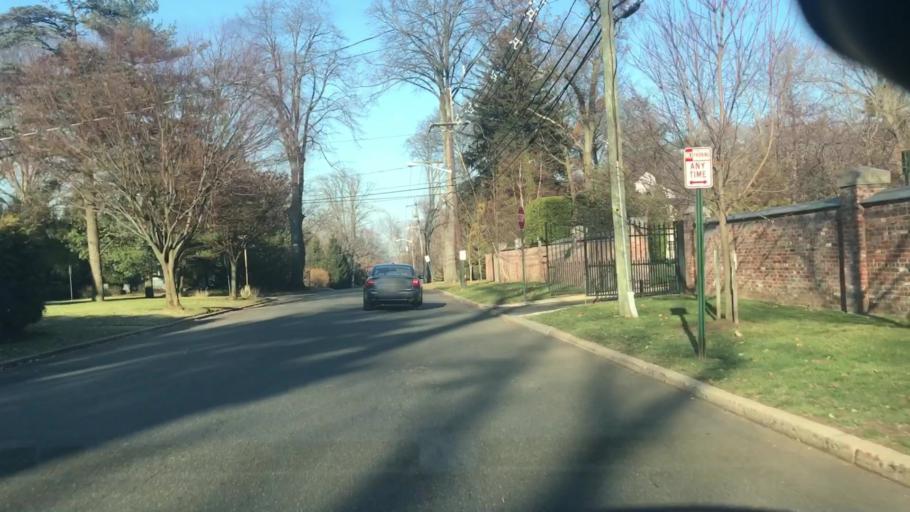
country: US
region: New Jersey
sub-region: Bergen County
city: Englewood
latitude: 40.8827
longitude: -73.9736
